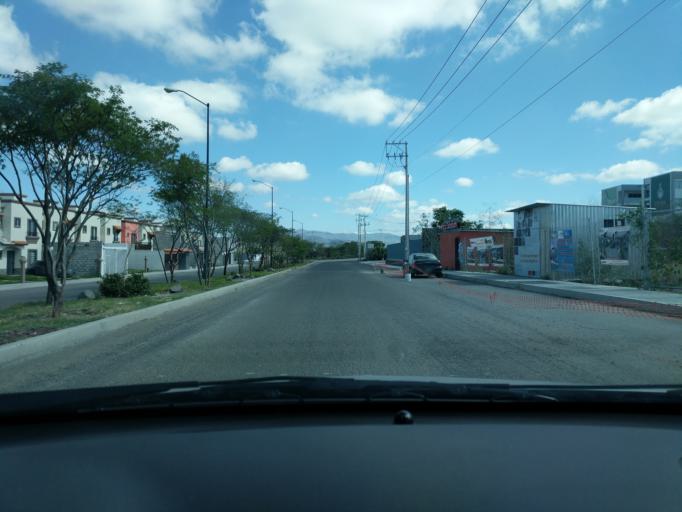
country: MX
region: Queretaro
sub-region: Queretaro
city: Patria Nueva
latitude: 20.6469
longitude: -100.4834
